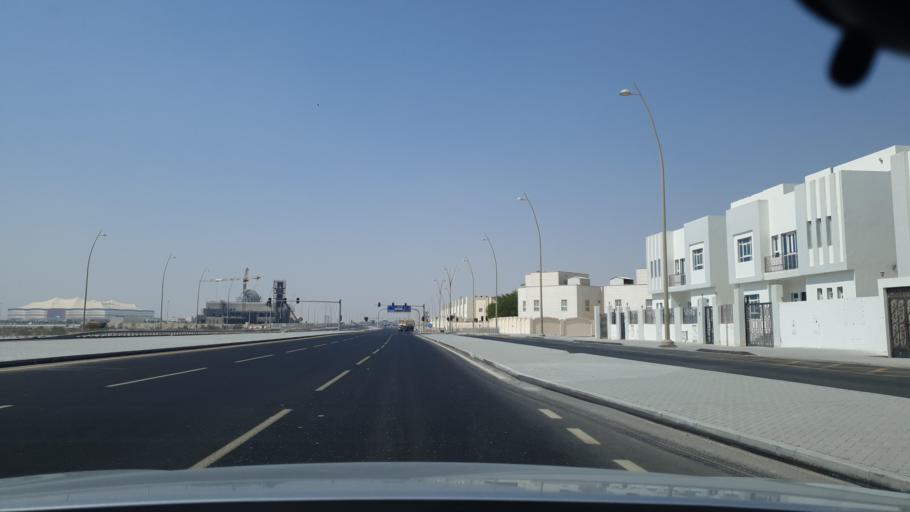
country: QA
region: Al Khawr
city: Al Khawr
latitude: 25.6653
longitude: 51.5090
